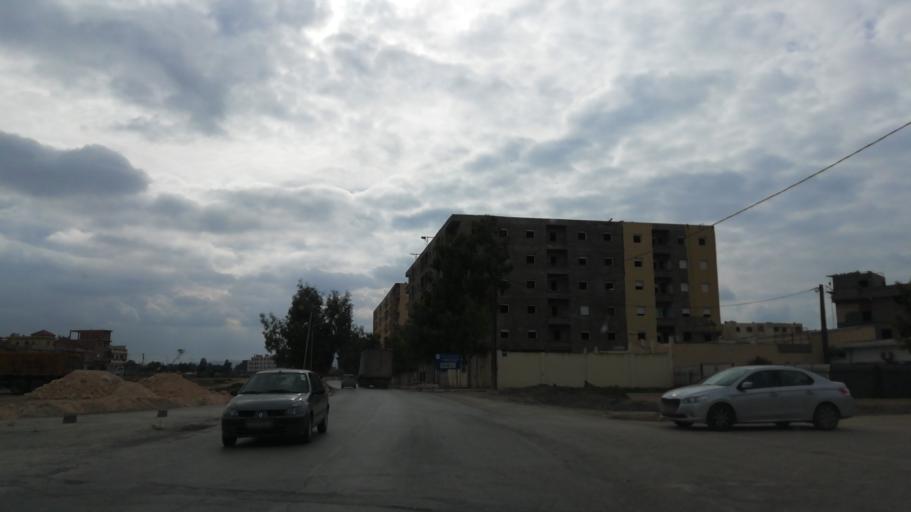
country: DZ
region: Oran
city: Sidi ech Chahmi
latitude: 35.5579
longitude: -0.4481
